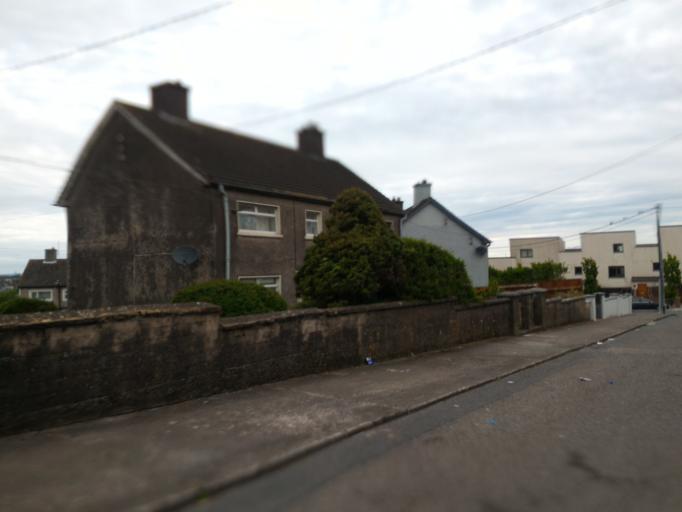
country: IE
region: Munster
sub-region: County Cork
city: Cork
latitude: 51.9105
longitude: -8.4632
